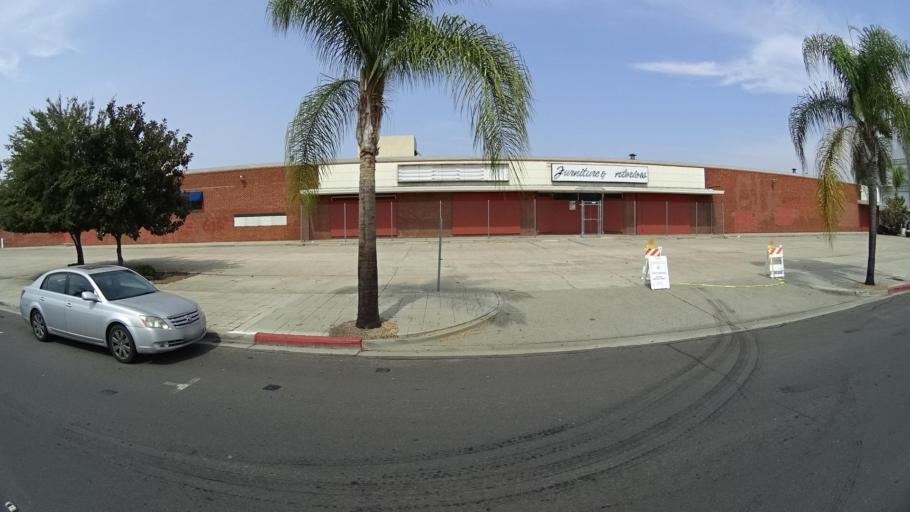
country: US
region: California
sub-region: San Diego County
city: Escondido
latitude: 33.1204
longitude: -117.0818
